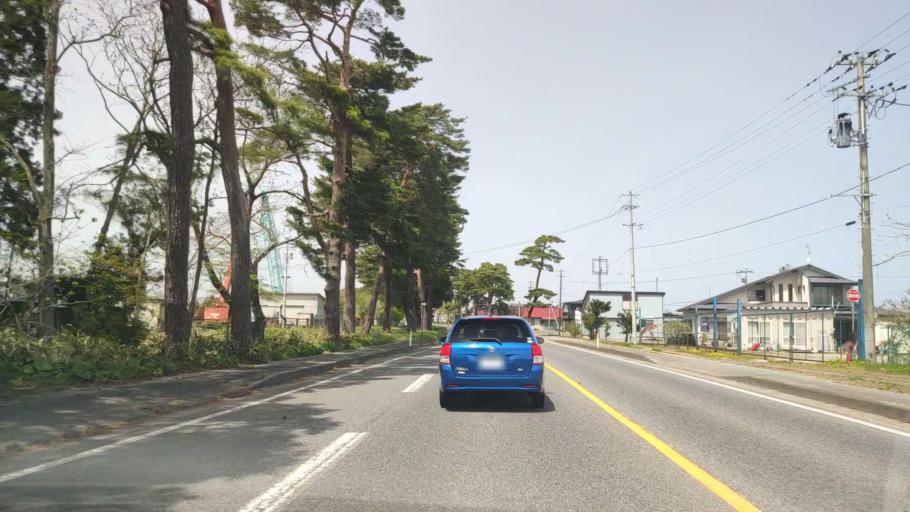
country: JP
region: Aomori
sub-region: Misawa Shi
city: Inuotose
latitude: 40.6694
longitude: 141.1843
